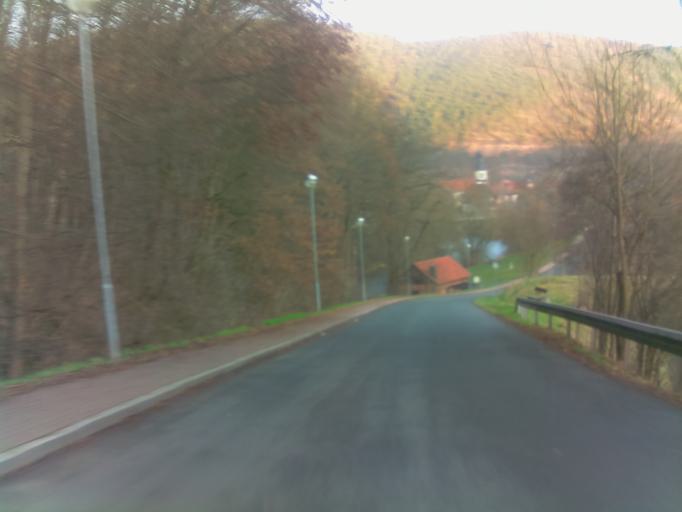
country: DE
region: Thuringia
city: Reinstadt
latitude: 50.7322
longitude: 11.4492
